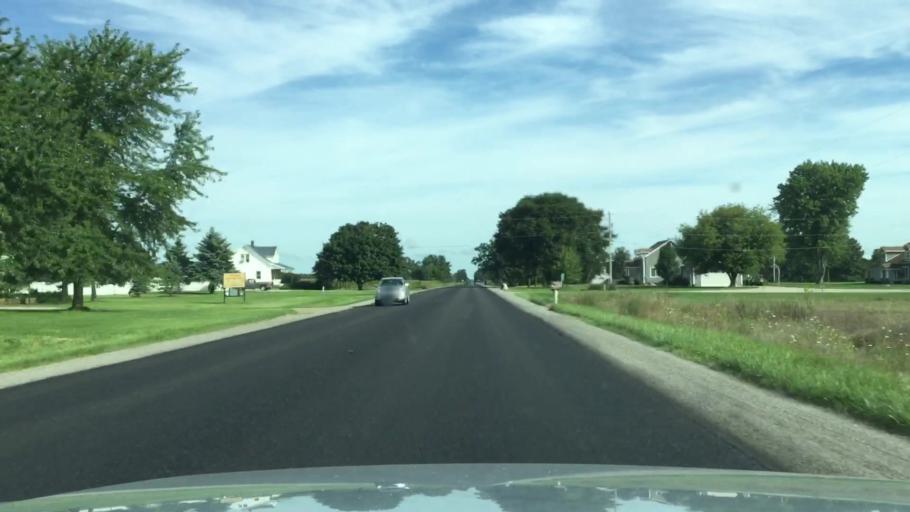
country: US
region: Michigan
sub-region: Genesee County
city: Montrose
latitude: 43.1369
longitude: -83.9292
